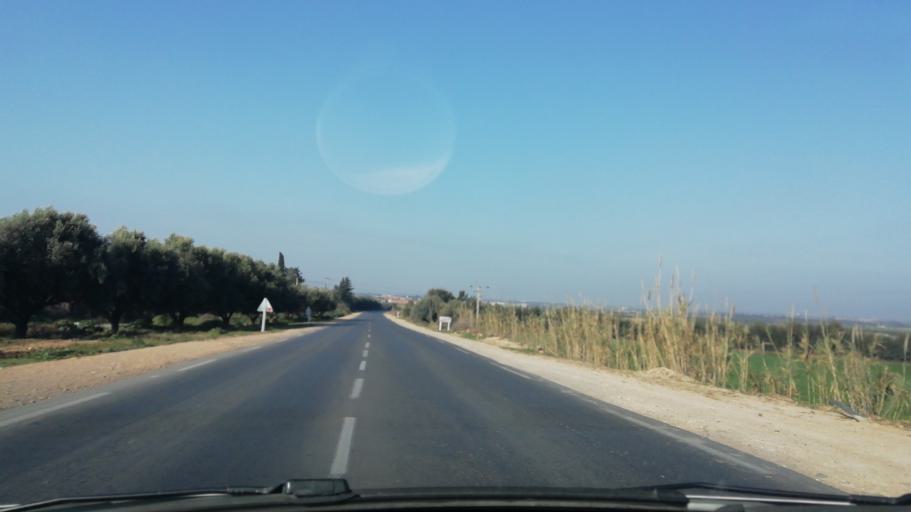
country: DZ
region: Mostaganem
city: Mostaganem
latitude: 35.7544
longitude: 0.1961
